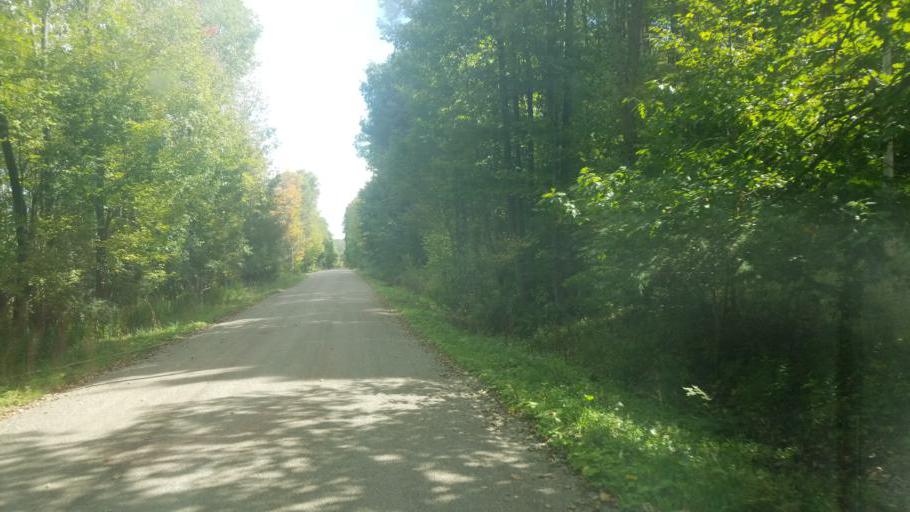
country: US
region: New York
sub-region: Allegany County
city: Cuba
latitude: 42.1928
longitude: -78.3195
